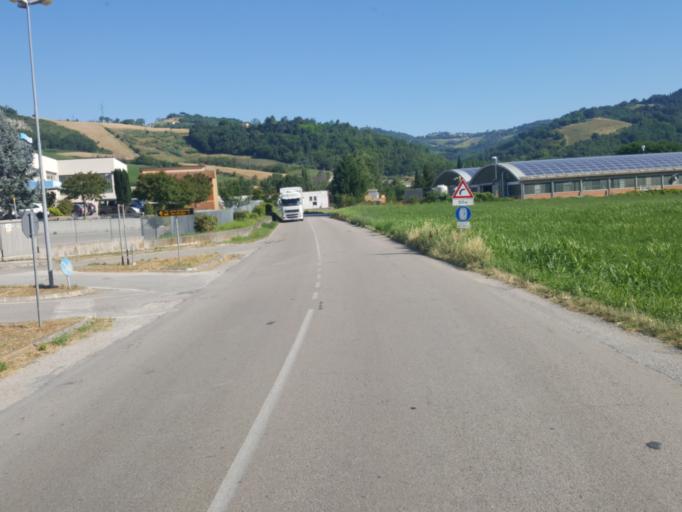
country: IT
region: The Marches
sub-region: Provincia di Pesaro e Urbino
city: Borgo Massano
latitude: 43.8250
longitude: 12.6809
